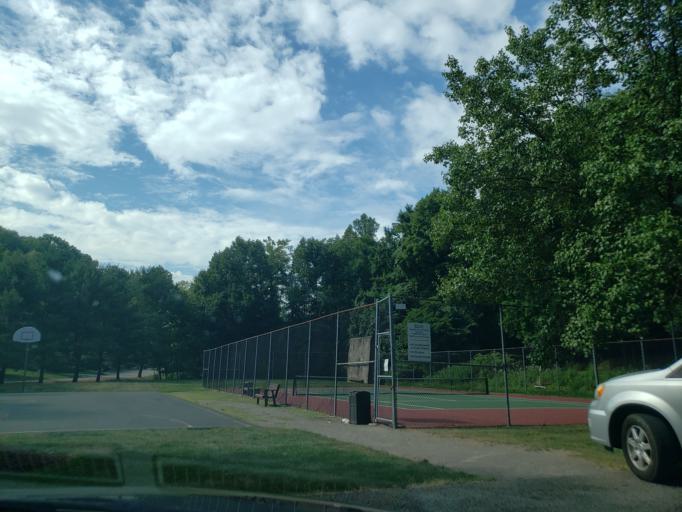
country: US
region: Pennsylvania
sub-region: Allegheny County
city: Coraopolis
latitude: 40.5405
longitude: -80.1489
